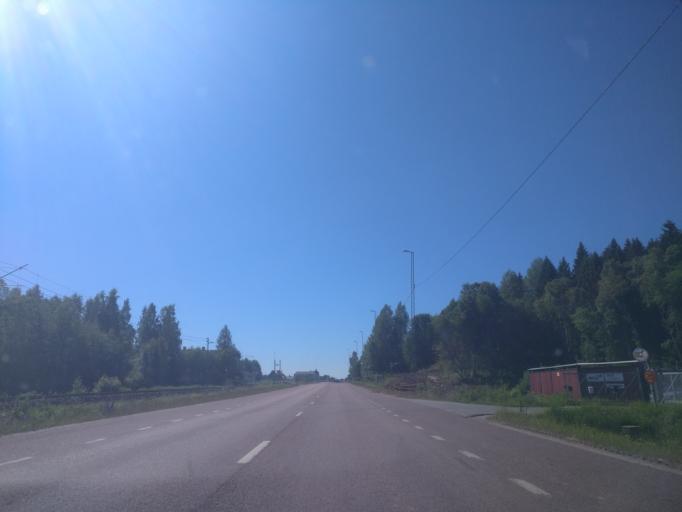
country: SE
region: Vaesternorrland
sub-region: Sundsvalls Kommun
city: Nolby
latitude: 62.2791
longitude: 17.3771
